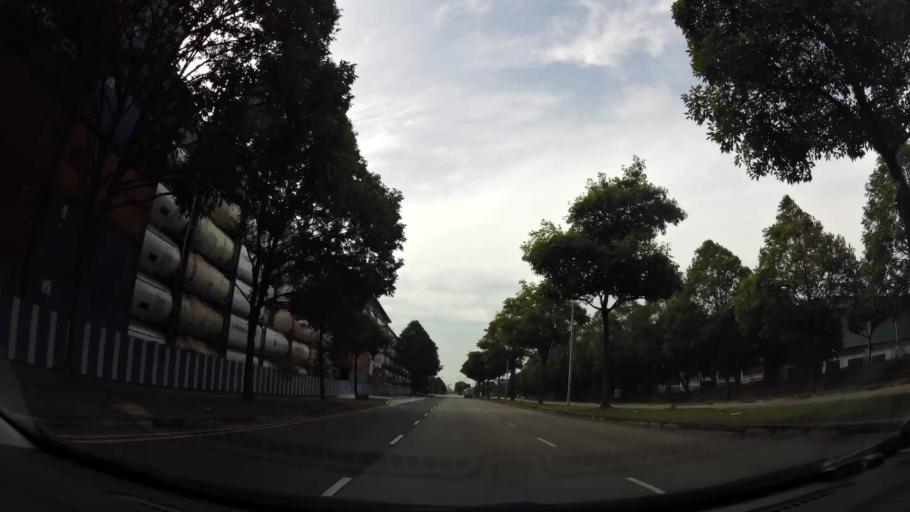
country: MY
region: Johor
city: Johor Bahru
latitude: 1.2909
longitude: 103.6314
